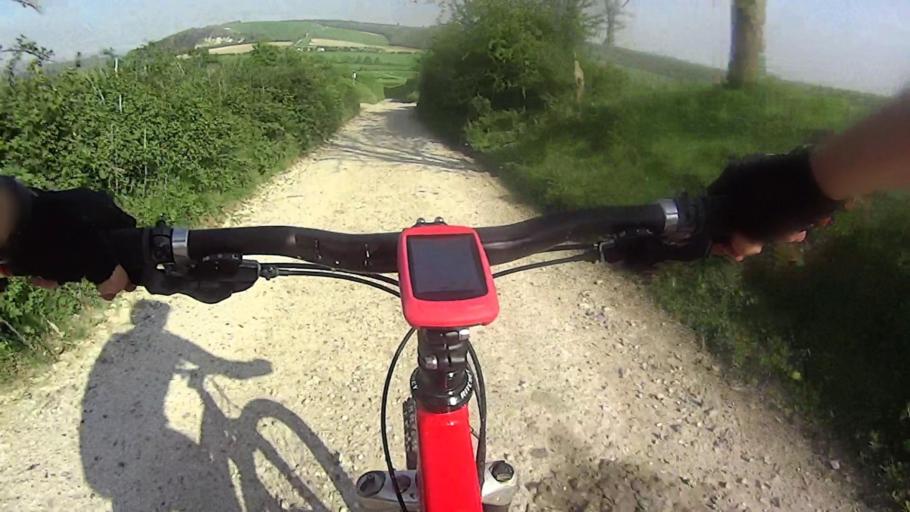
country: GB
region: England
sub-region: West Sussex
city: Midhurst
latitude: 50.9433
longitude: -0.7680
